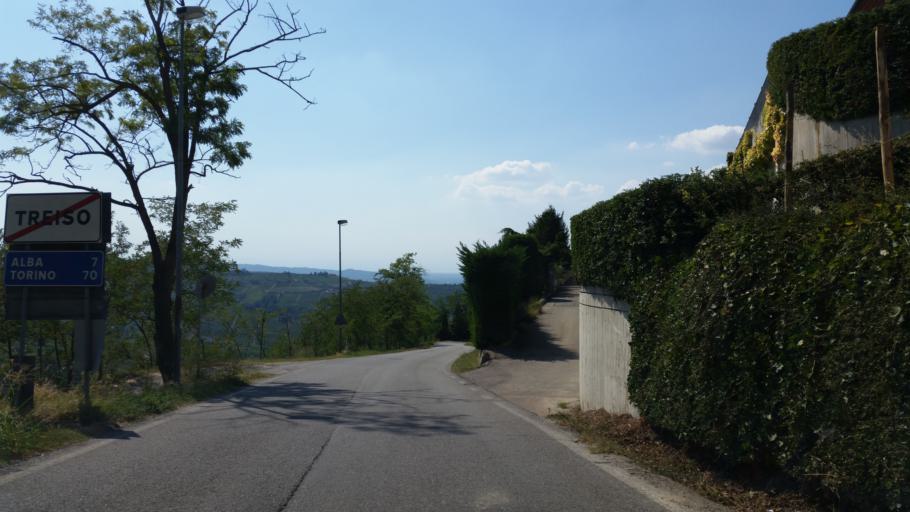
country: IT
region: Piedmont
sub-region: Provincia di Cuneo
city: Treiso
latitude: 44.6883
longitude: 8.0863
